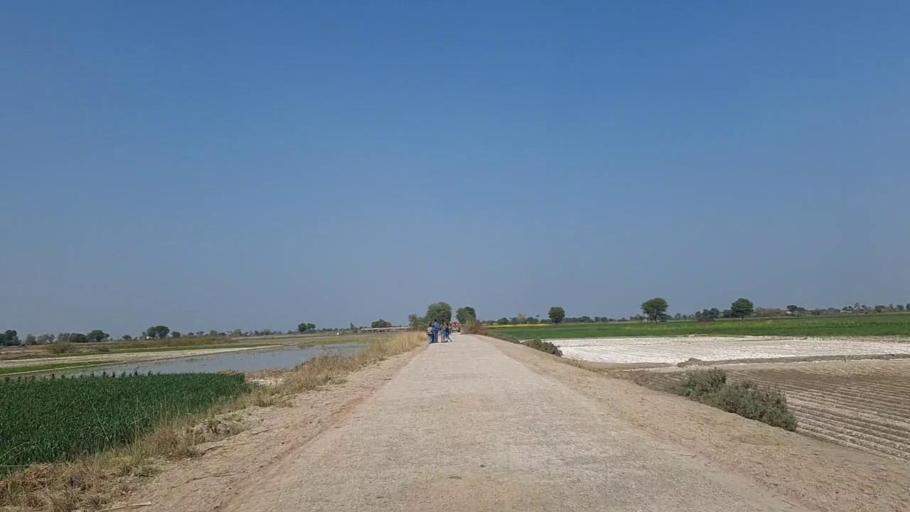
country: PK
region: Sindh
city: Nawabshah
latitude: 26.2684
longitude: 68.5133
